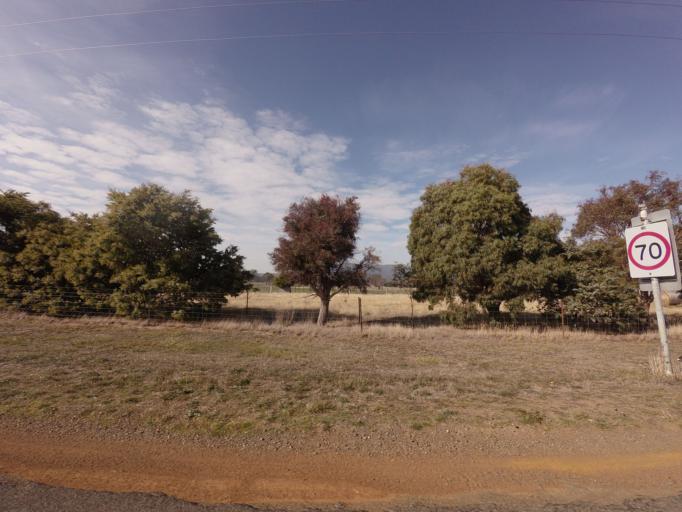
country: AU
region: Tasmania
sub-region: Sorell
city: Sorell
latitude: -42.4523
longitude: 147.4617
